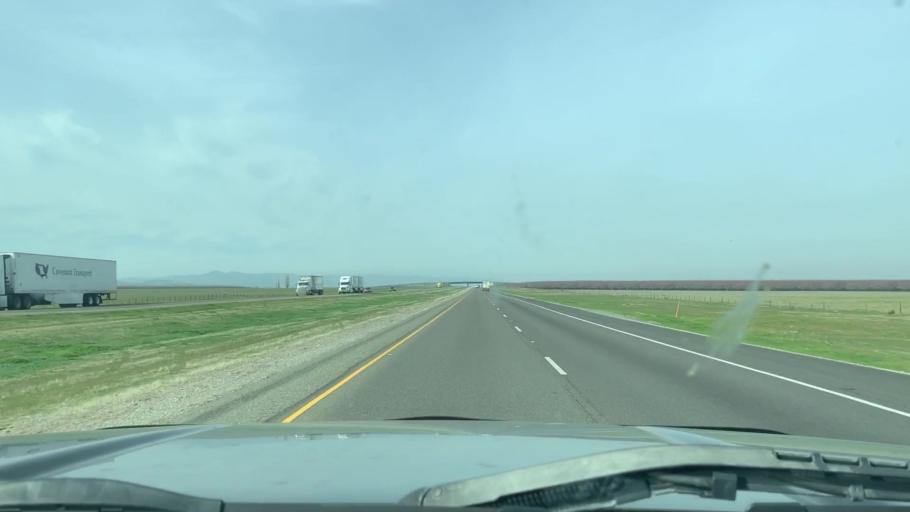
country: US
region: California
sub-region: Fresno County
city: Mendota
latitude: 36.5707
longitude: -120.5407
